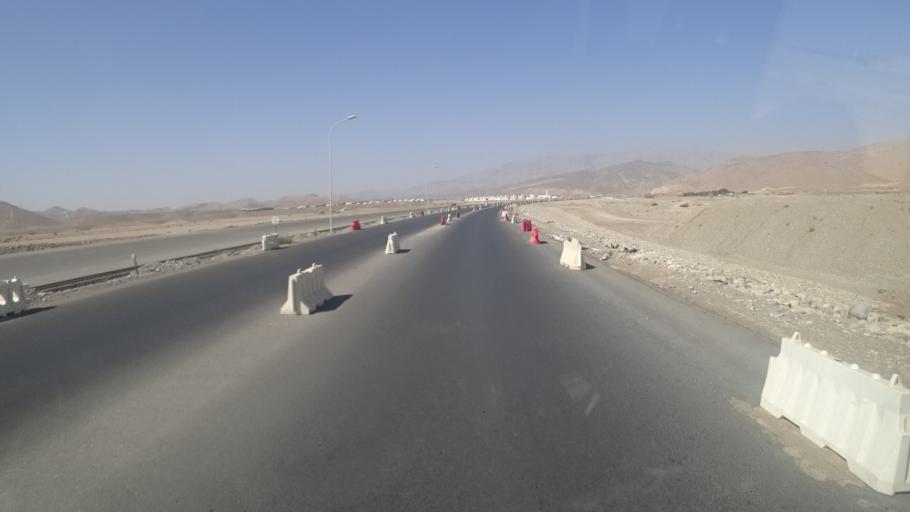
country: OM
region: Ash Sharqiyah
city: Sur
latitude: 22.5178
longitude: 59.4569
